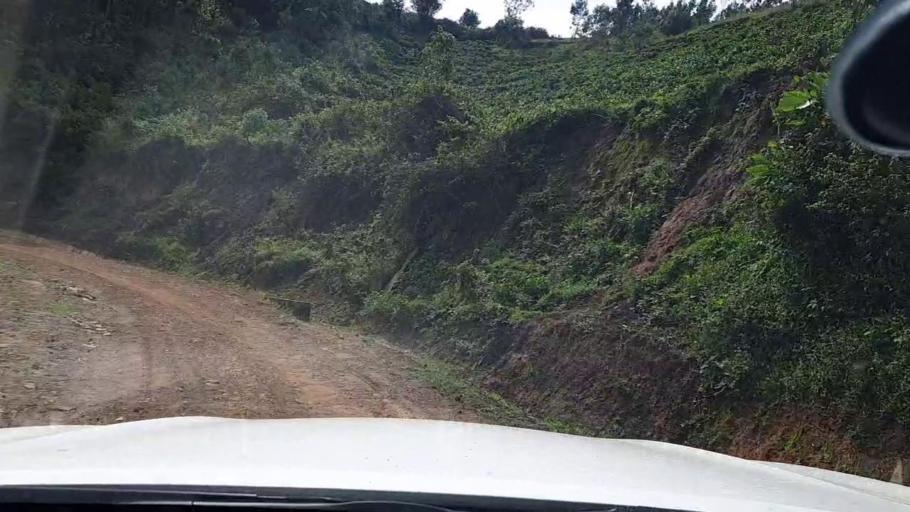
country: RW
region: Western Province
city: Kibuye
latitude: -2.1393
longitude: 29.3765
